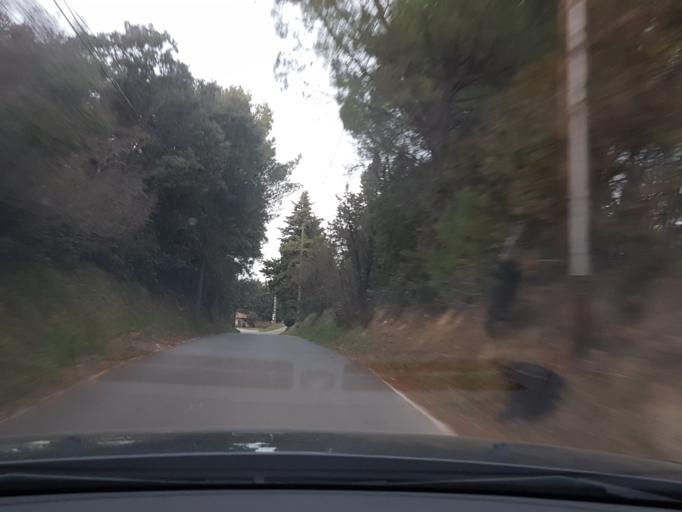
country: FR
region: Provence-Alpes-Cote d'Azur
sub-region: Departement du Vaucluse
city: Loriol-du-Comtat
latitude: 44.0838
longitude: 4.9964
